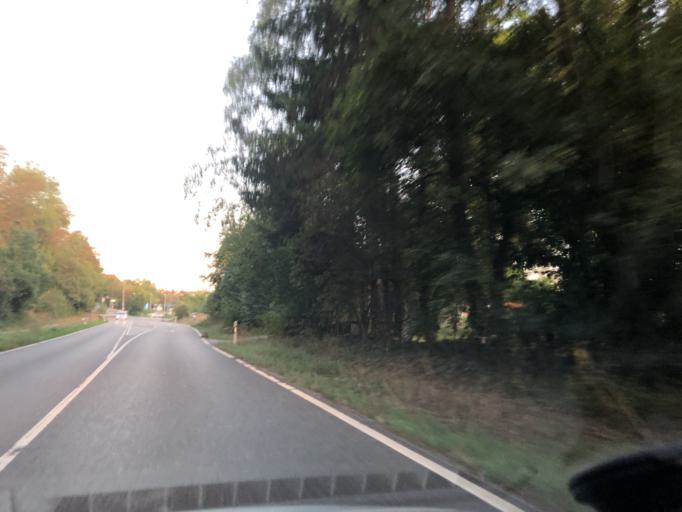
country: DE
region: Baden-Wuerttemberg
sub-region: Regierungsbezirk Stuttgart
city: Marbach am Neckar
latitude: 48.8919
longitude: 9.2688
